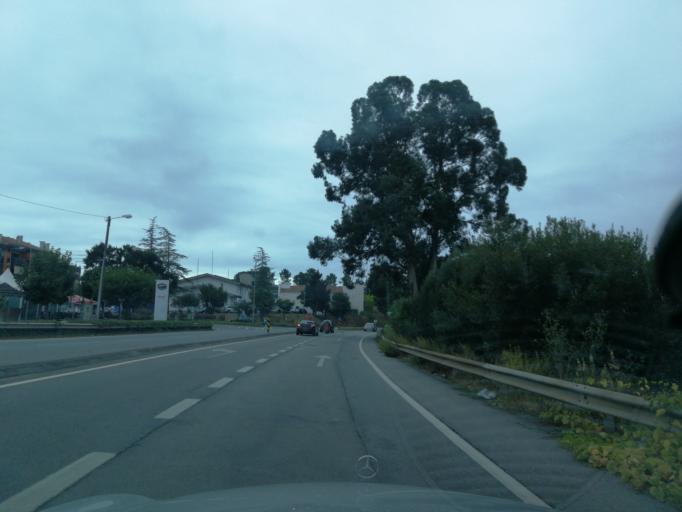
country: PT
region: Aveiro
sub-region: Agueda
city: Agueda
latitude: 40.5860
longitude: -8.4491
